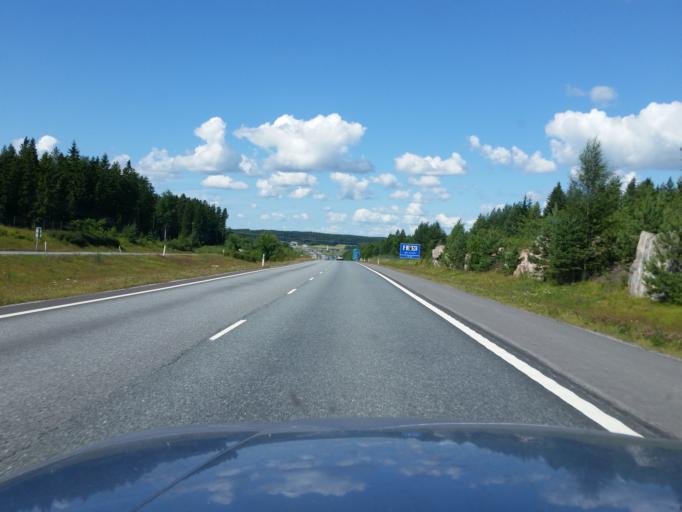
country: FI
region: Varsinais-Suomi
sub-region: Salo
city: Pertteli
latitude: 60.4083
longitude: 23.2096
